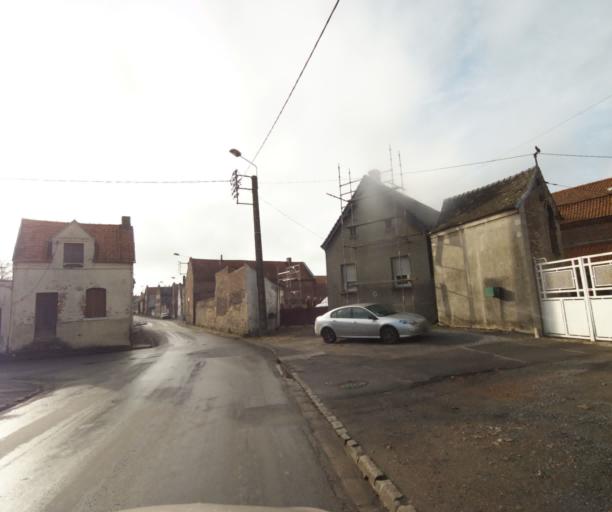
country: FR
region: Nord-Pas-de-Calais
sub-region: Departement du Nord
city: Vendegies-sur-Ecaillon
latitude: 50.2690
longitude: 3.4768
